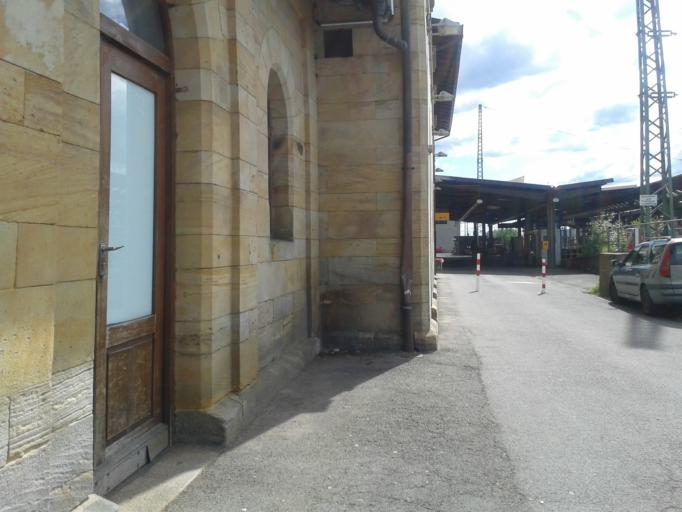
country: DE
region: Bavaria
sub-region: Upper Franconia
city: Lichtenfels
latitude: 50.1464
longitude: 11.0599
